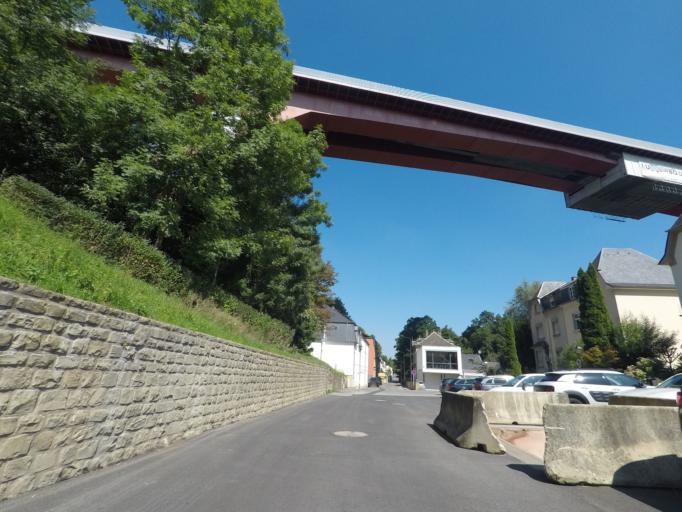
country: LU
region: Luxembourg
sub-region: Canton de Luxembourg
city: Luxembourg
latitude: 49.6170
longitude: 6.1309
